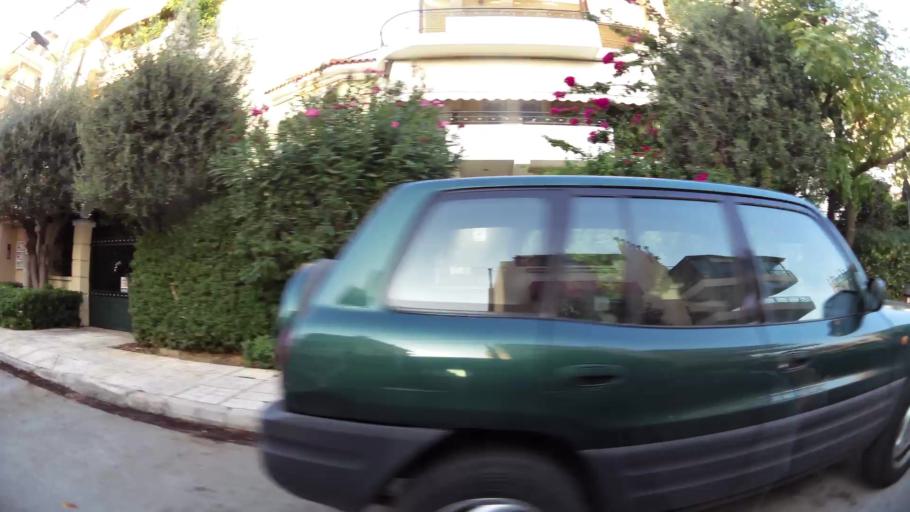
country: GR
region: Attica
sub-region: Nomarchia Athinas
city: Argyroupoli
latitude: 37.8902
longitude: 23.7630
